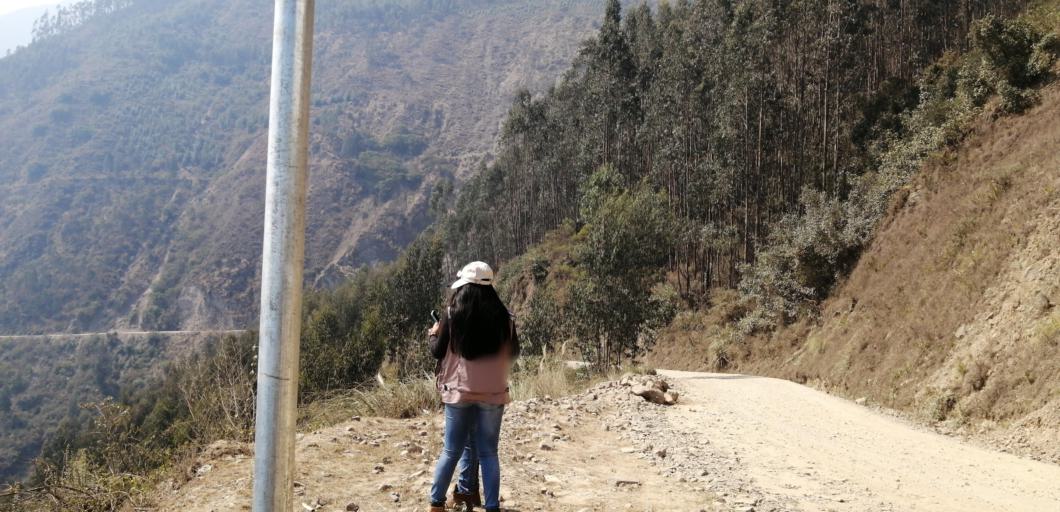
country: BO
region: La Paz
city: Quime
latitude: -16.9025
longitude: -67.1460
